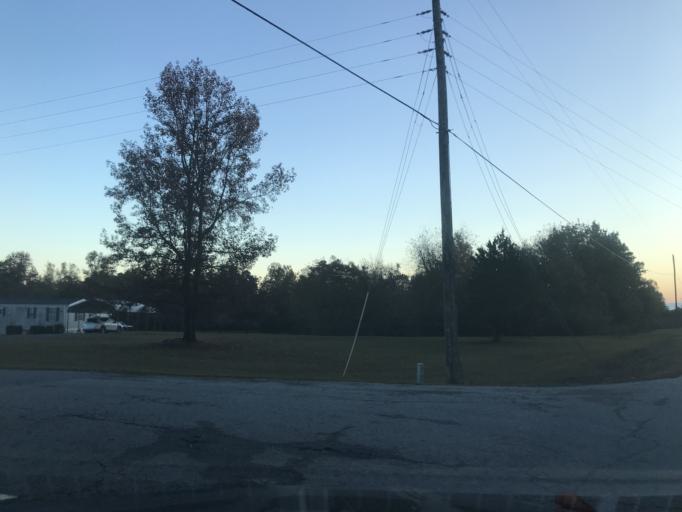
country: US
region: South Carolina
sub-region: Spartanburg County
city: Mayo
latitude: 35.1189
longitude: -81.7740
